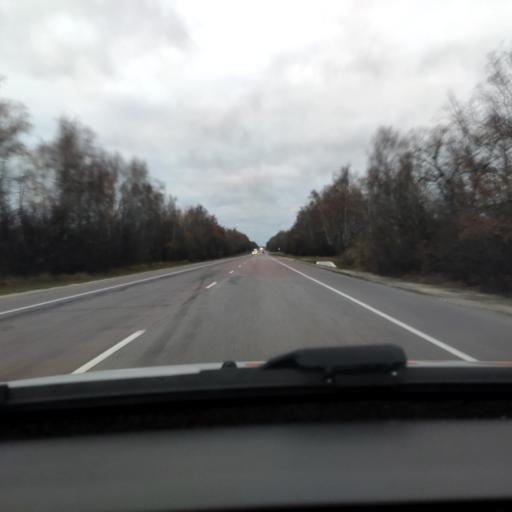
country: RU
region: Lipetsk
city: Khlevnoye
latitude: 52.2946
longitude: 39.1673
